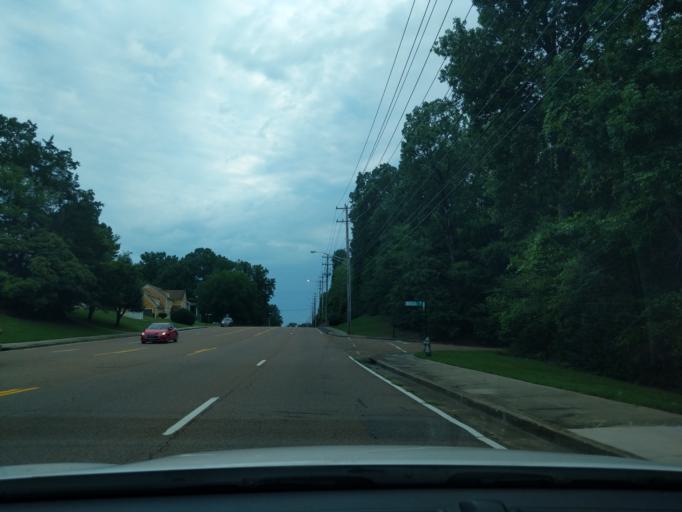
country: US
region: Tennessee
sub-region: Shelby County
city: Germantown
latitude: 35.0821
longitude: -89.8117
